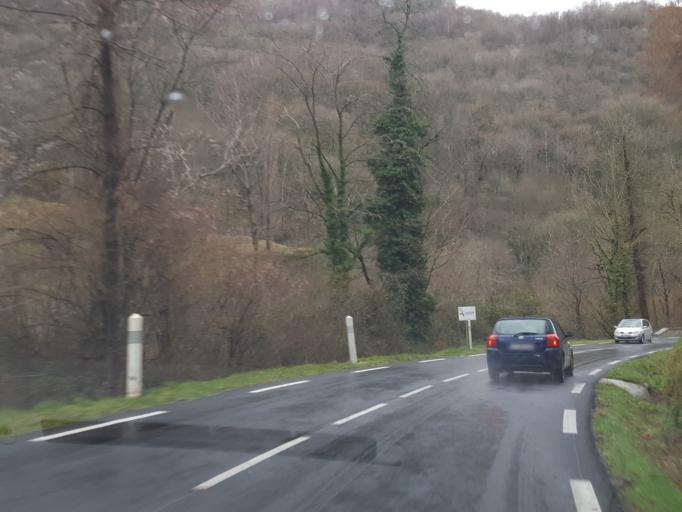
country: FR
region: Midi-Pyrenees
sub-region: Departement de l'Ariege
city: Saint-Girons
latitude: 42.9296
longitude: 1.1826
